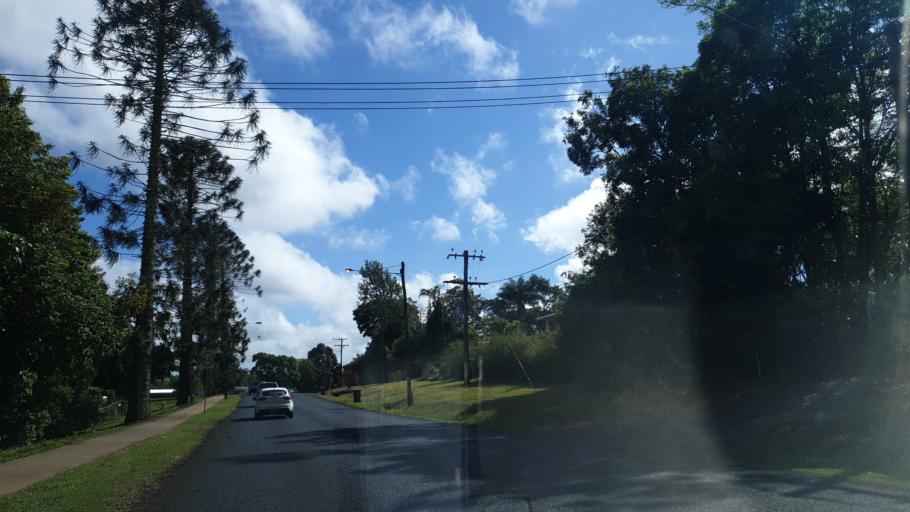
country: AU
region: Queensland
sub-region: Tablelands
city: Atherton
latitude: -17.3535
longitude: 145.5885
